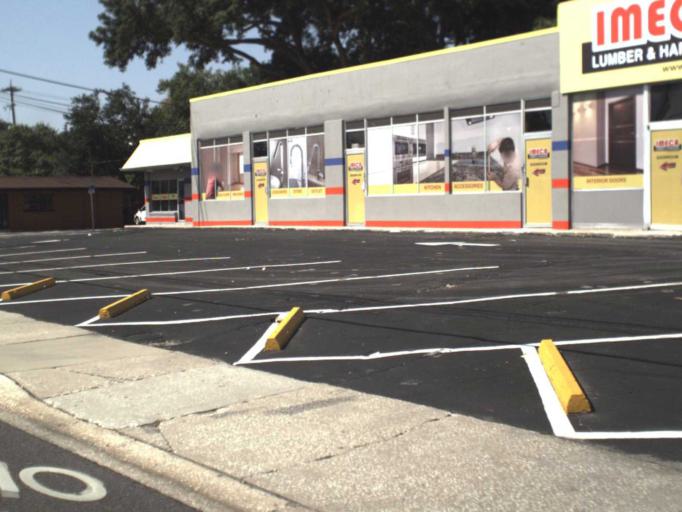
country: US
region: Florida
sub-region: Hillsborough County
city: Carrollwood
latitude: 28.0298
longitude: -82.4596
